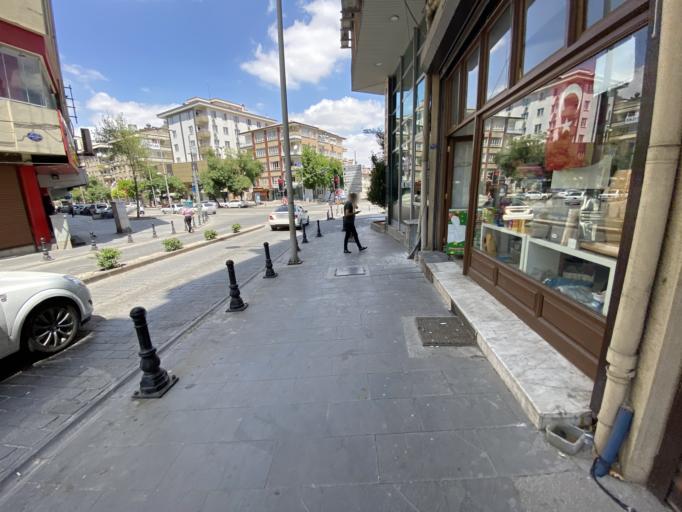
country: TR
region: Gaziantep
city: Gaziantep
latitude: 37.0620
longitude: 37.3754
